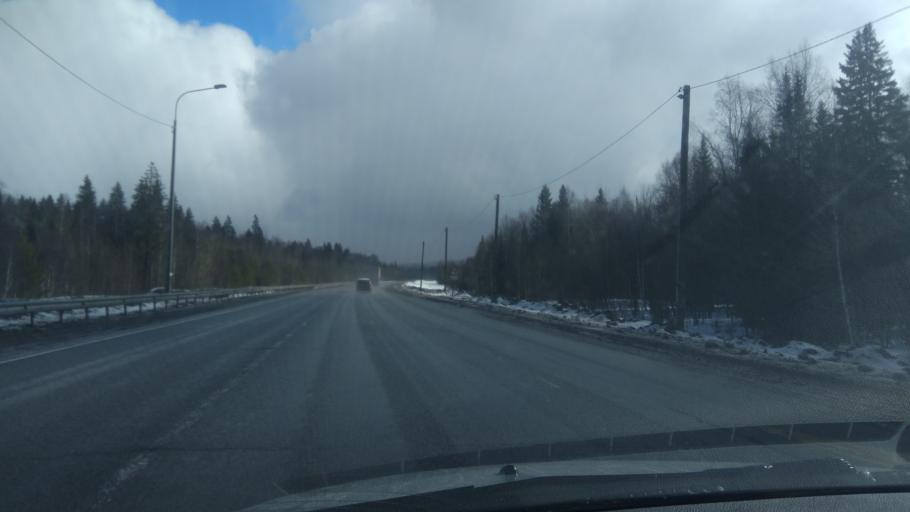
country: RU
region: Sverdlovsk
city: Arti
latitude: 56.7940
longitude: 58.4879
